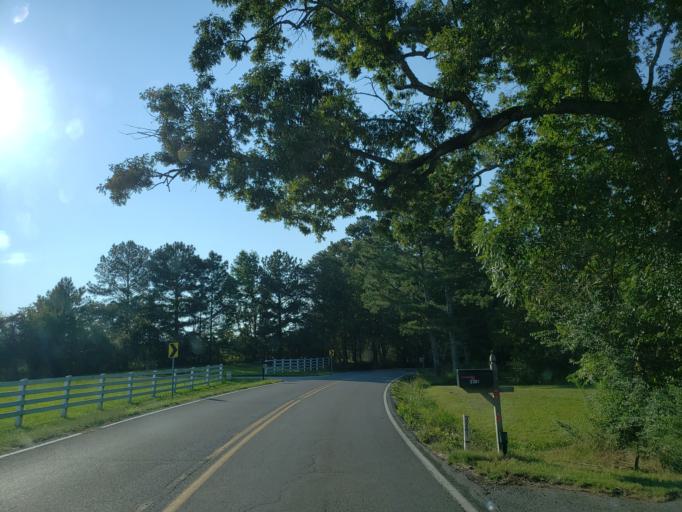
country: US
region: Tennessee
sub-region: Bradley County
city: Wildwood Lake
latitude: 35.0689
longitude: -84.7752
